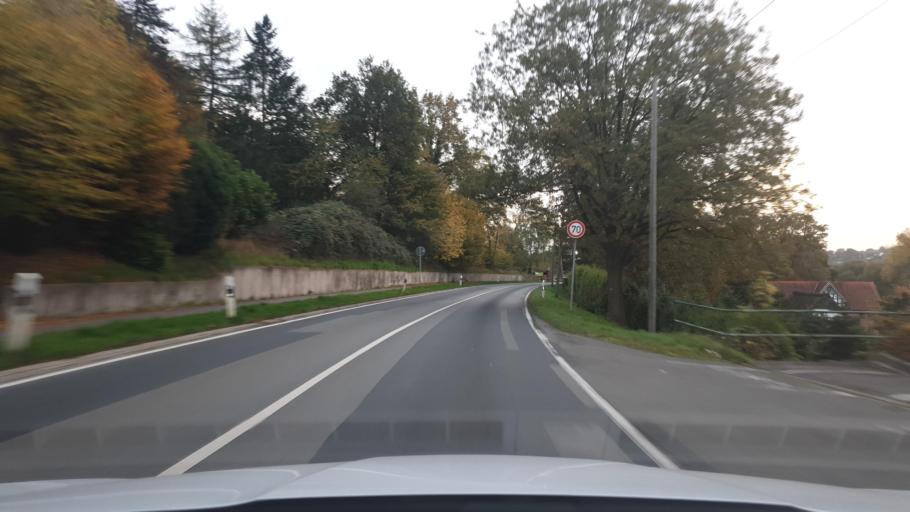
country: DE
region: North Rhine-Westphalia
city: Loehne
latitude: 52.1547
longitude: 8.6810
